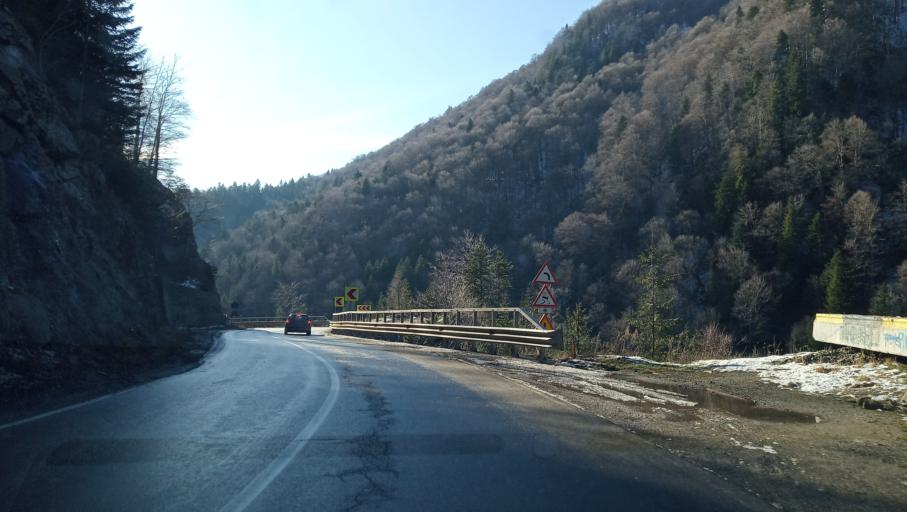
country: RO
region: Brasov
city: Crivina
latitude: 45.4726
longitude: 25.9210
